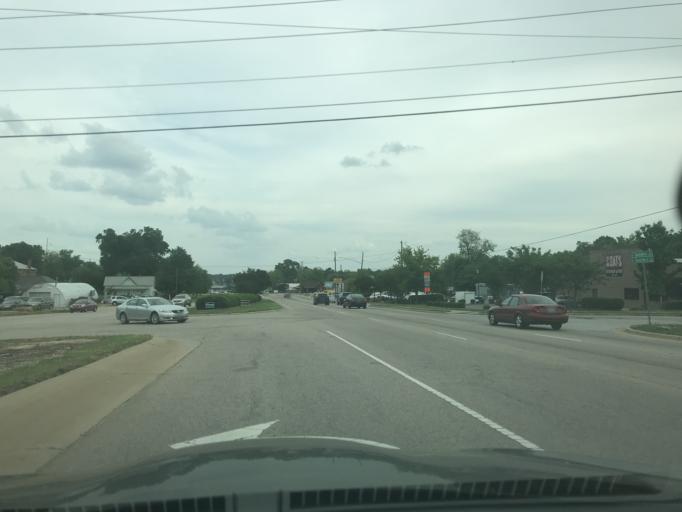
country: US
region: North Carolina
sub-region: Wake County
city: Raleigh
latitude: 35.7632
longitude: -78.6491
